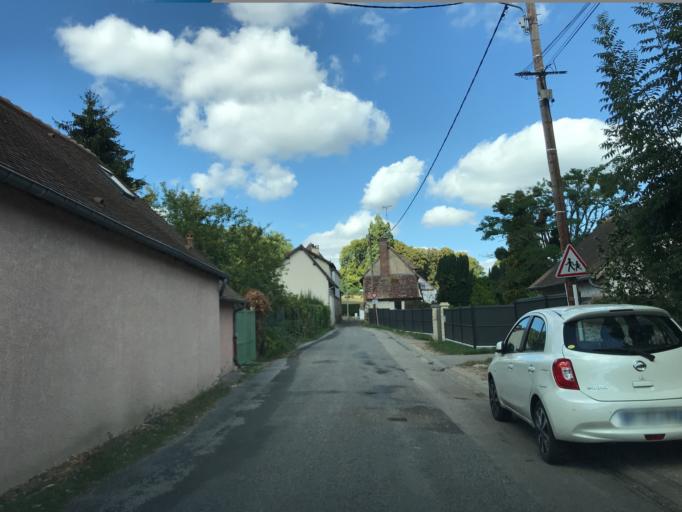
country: FR
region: Haute-Normandie
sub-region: Departement de l'Eure
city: La Chapelle-Reanville
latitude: 49.1386
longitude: 1.4039
